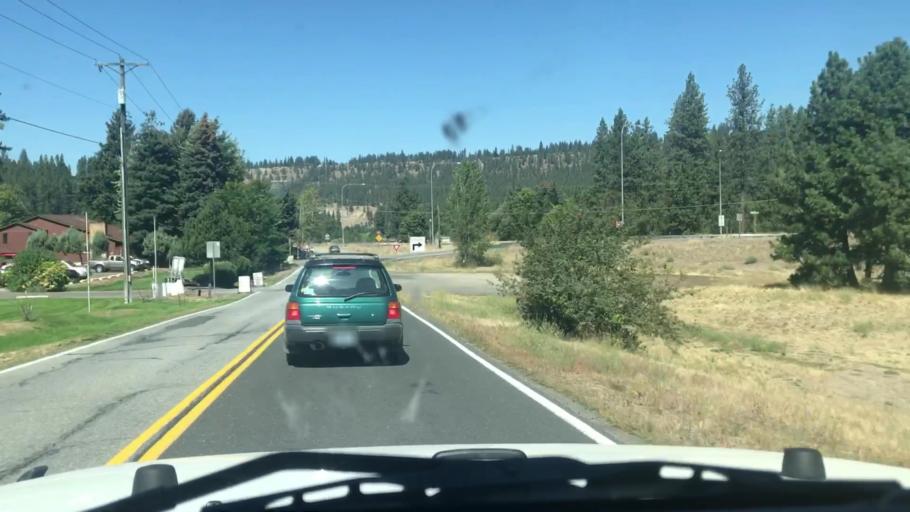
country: US
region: Washington
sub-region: Spokane County
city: Spokane
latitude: 47.6007
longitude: -117.4120
